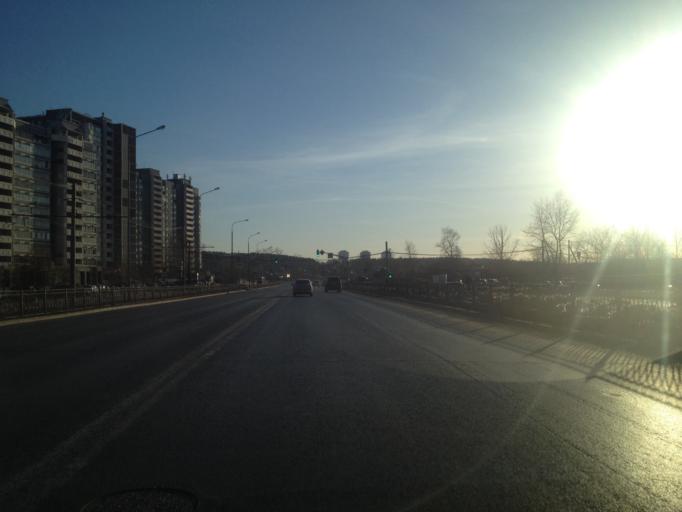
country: RU
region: Sverdlovsk
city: Sovkhoznyy
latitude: 56.8231
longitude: 60.5408
